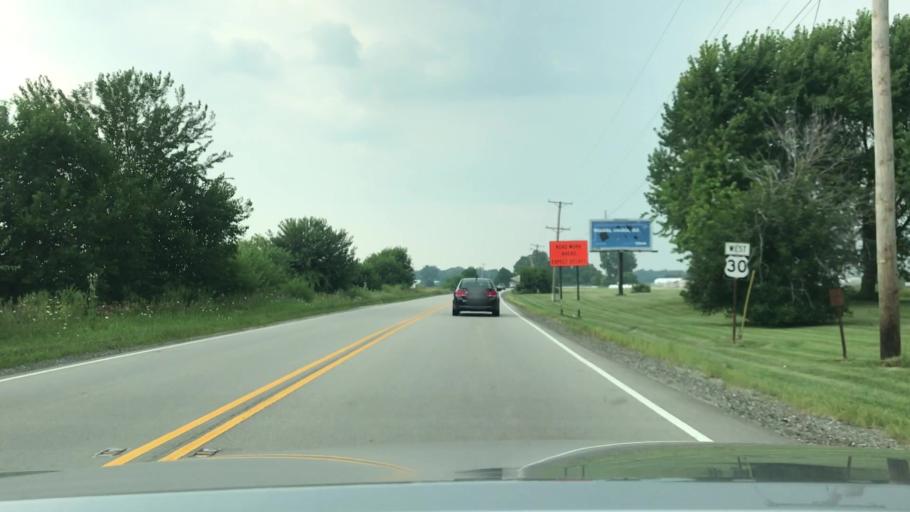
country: US
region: Illinois
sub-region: Will County
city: Plainfield
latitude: 41.6548
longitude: -88.2330
